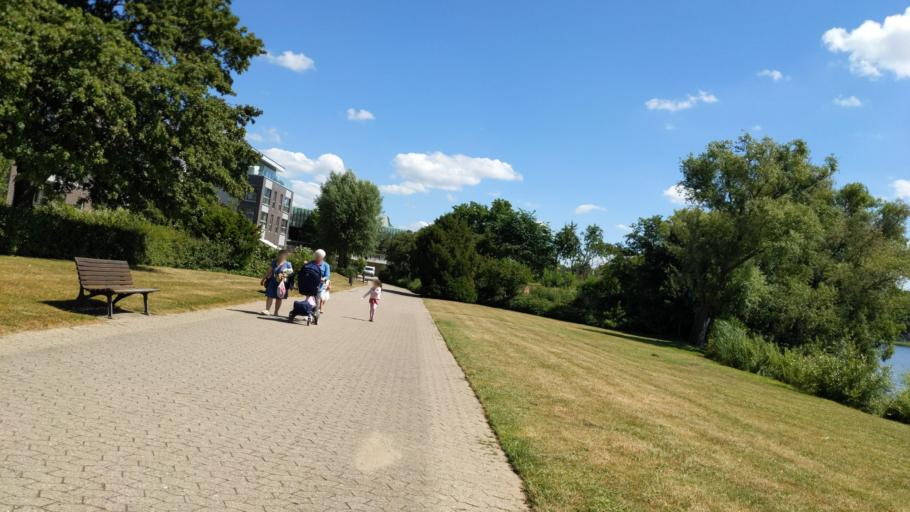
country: DE
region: Schleswig-Holstein
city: Ratzeburg
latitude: 53.6959
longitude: 10.7737
